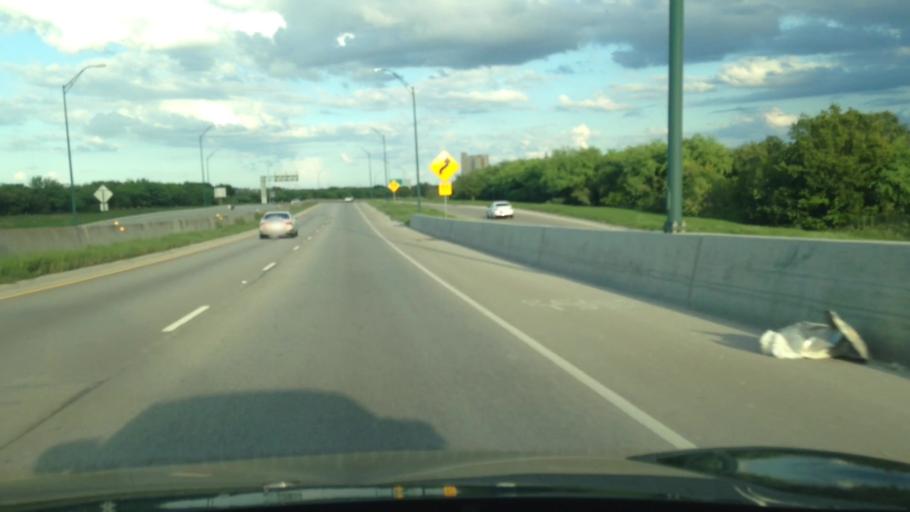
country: US
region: Texas
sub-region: Bexar County
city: Windcrest
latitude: 29.5374
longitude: -98.4100
